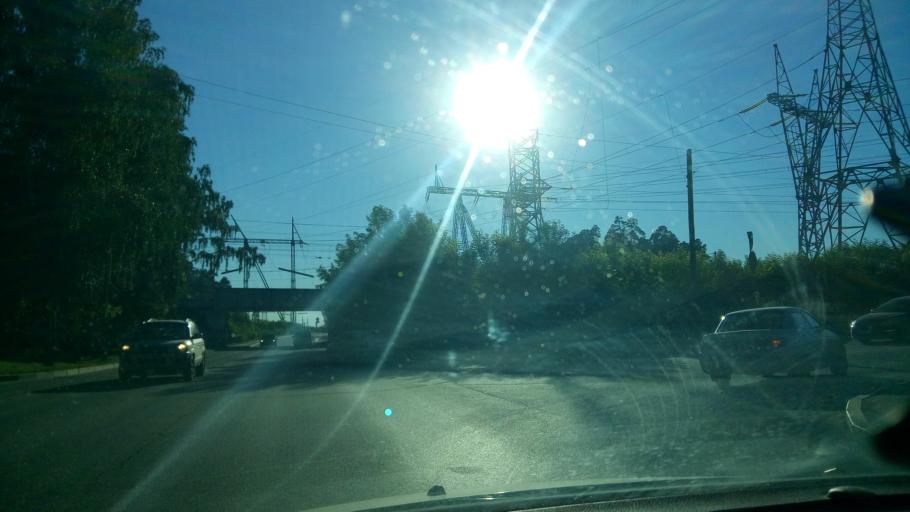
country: RU
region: Sverdlovsk
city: Istok
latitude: 56.7800
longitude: 60.7914
